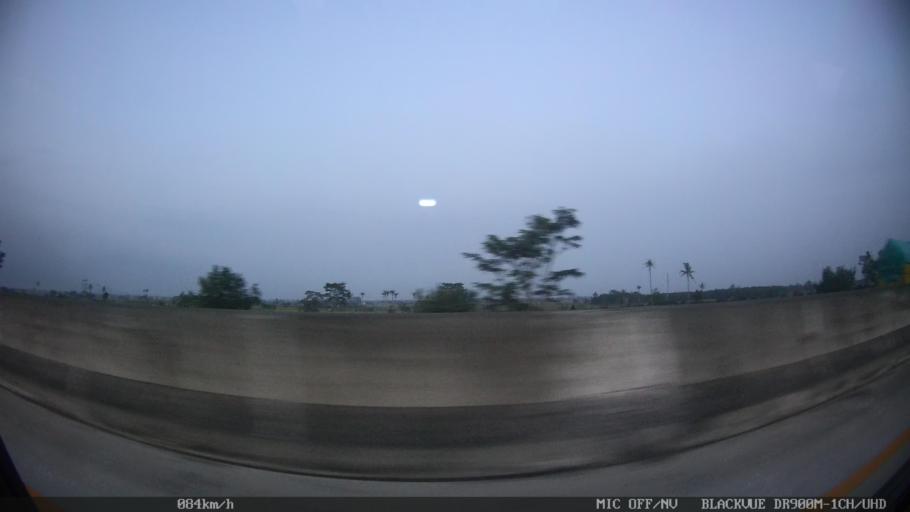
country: ID
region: Lampung
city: Sidorejo
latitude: -5.6150
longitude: 105.5600
